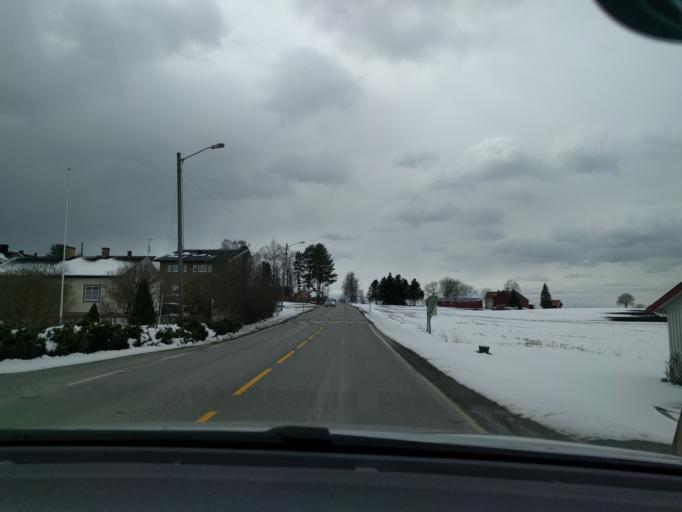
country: NO
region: Hedmark
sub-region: Stange
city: Stange
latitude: 60.7161
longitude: 11.1813
